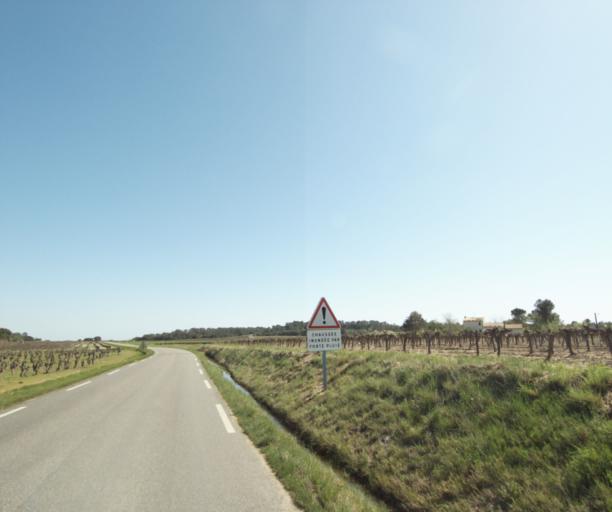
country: FR
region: Languedoc-Roussillon
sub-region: Departement de l'Herault
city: Saint-Drezery
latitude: 43.7490
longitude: 3.9620
